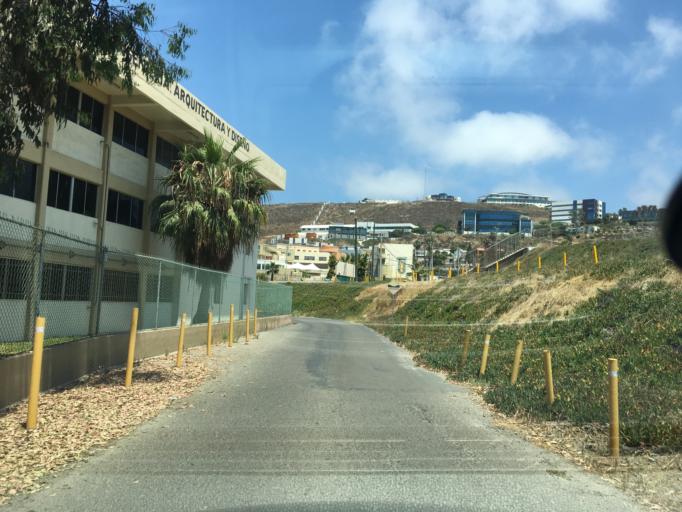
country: MX
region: Baja California
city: El Sauzal
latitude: 31.8657
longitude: -116.6680
